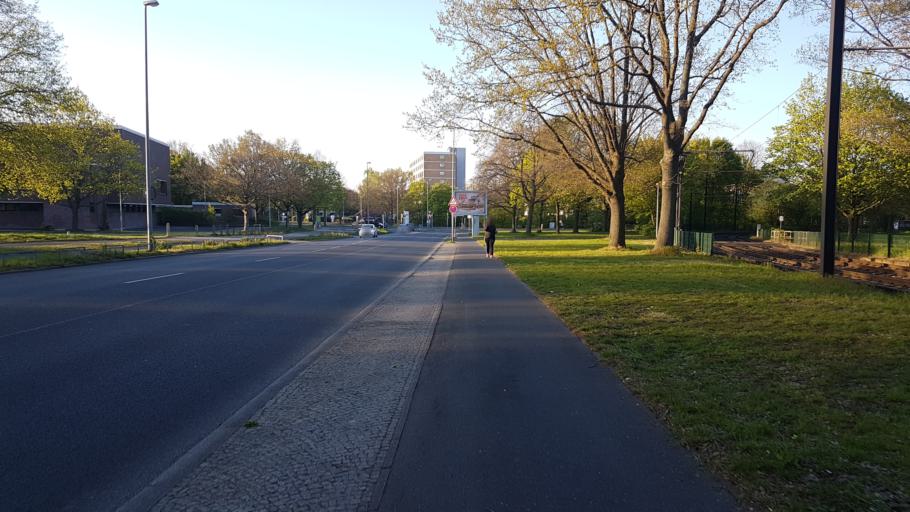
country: DE
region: Lower Saxony
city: Langenhagen
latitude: 52.4099
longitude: 9.7408
